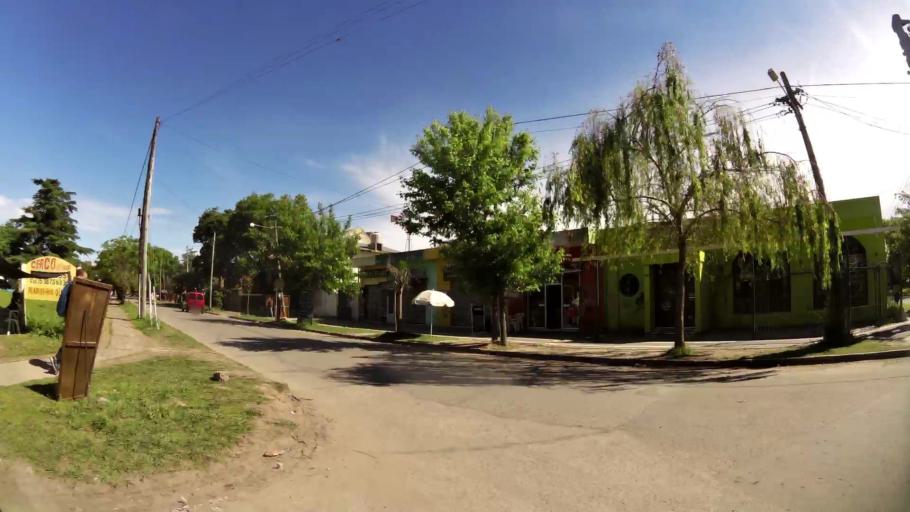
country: AR
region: Buenos Aires
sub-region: Partido de Almirante Brown
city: Adrogue
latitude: -34.7974
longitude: -58.3568
